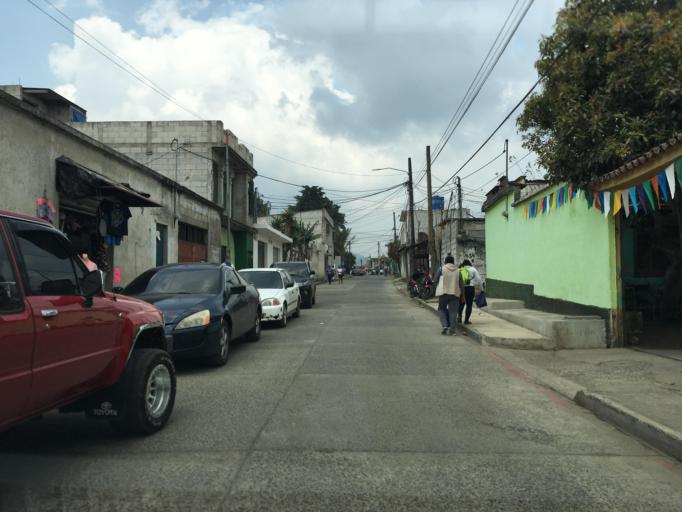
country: GT
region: Guatemala
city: Villa Canales
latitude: 14.4072
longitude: -90.5450
